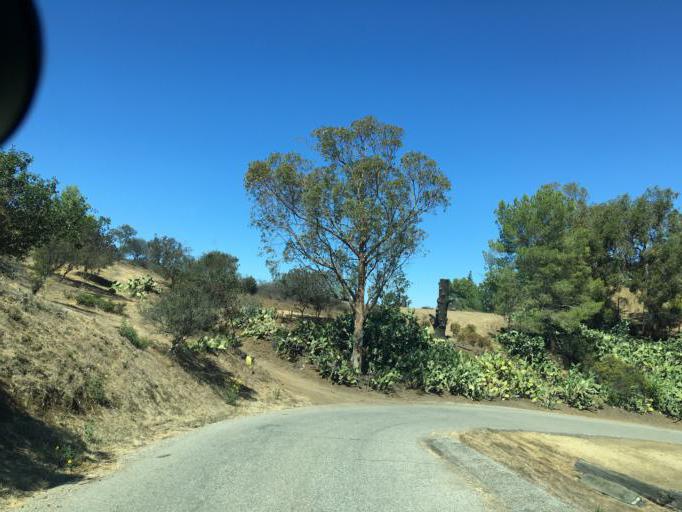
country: US
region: California
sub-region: Los Angeles County
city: Malibu
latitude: 34.0762
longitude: -118.8847
